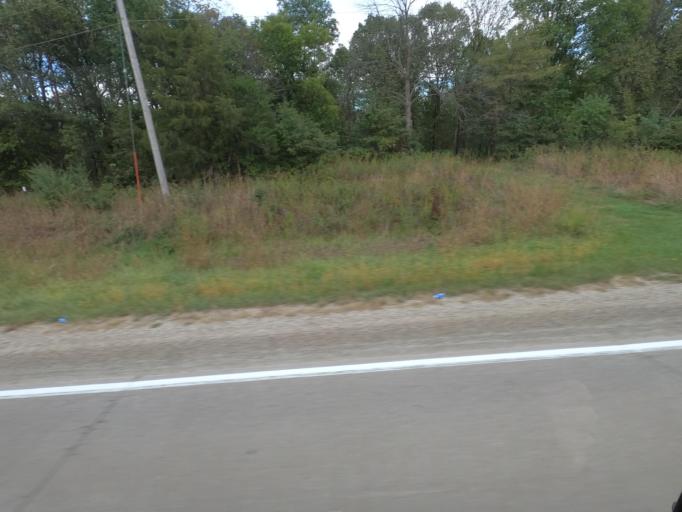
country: US
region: Iowa
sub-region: Henry County
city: Mount Pleasant
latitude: 40.7929
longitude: -91.7050
